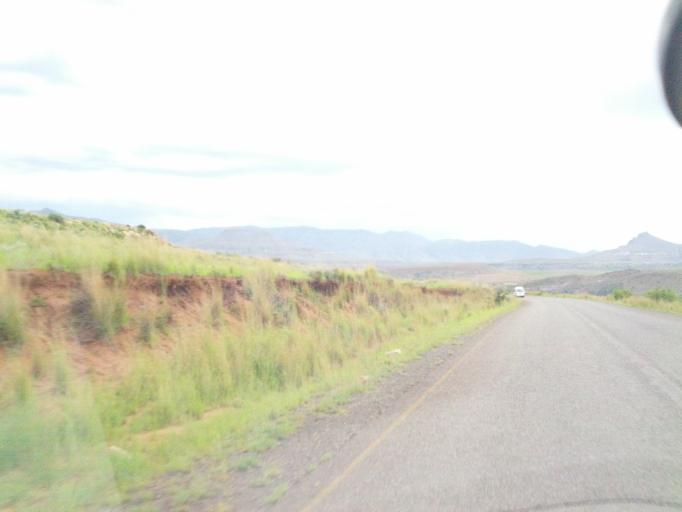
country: LS
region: Qacha's Nek
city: Qacha's Nek
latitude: -30.0506
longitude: 28.4943
